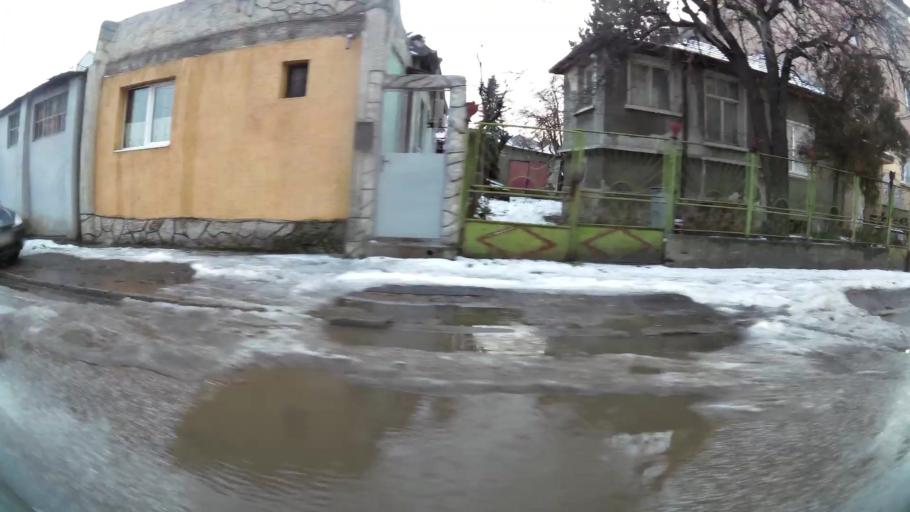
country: BG
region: Sofia-Capital
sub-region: Stolichna Obshtina
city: Sofia
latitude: 42.7177
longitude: 23.3425
